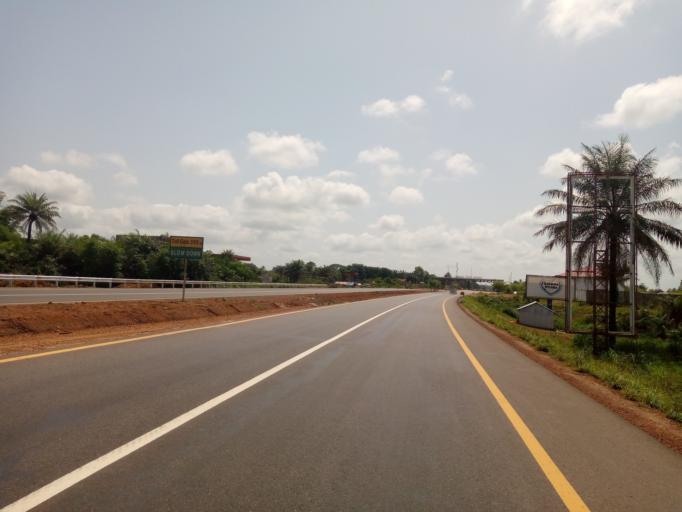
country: SL
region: Western Area
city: Waterloo
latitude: 8.3840
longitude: -12.9549
